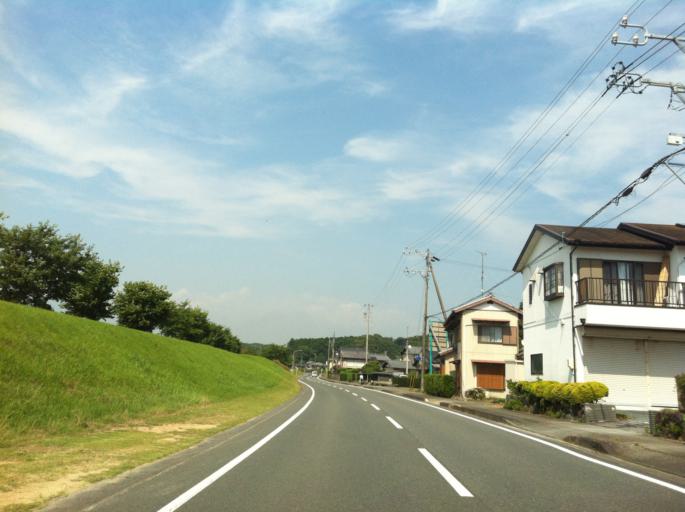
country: JP
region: Shizuoka
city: Mori
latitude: 34.7978
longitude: 137.9106
